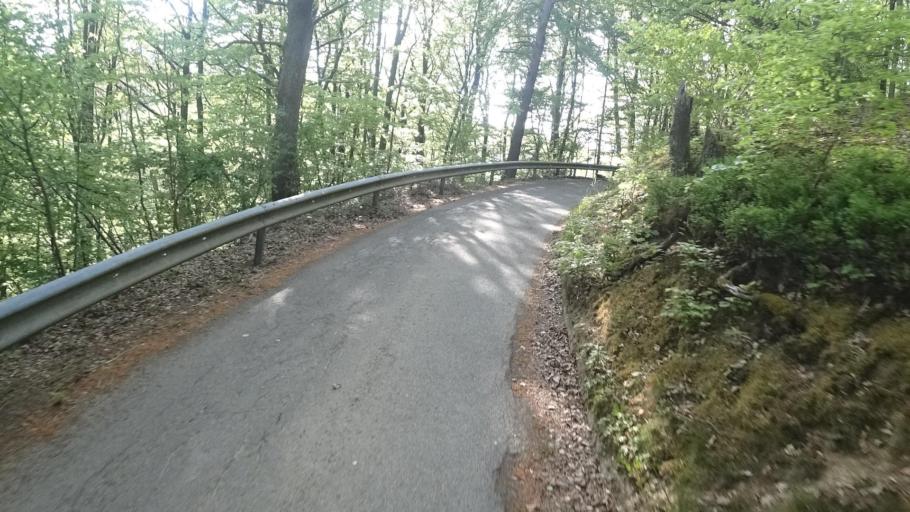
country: DE
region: Rheinland-Pfalz
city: Kirchsahr
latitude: 50.5074
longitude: 6.8721
